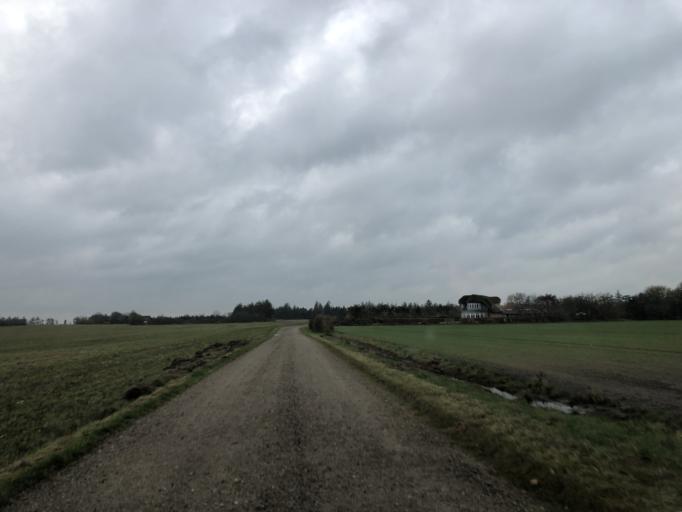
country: DK
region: Central Jutland
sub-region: Holstebro Kommune
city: Ulfborg
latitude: 56.3191
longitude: 8.2235
